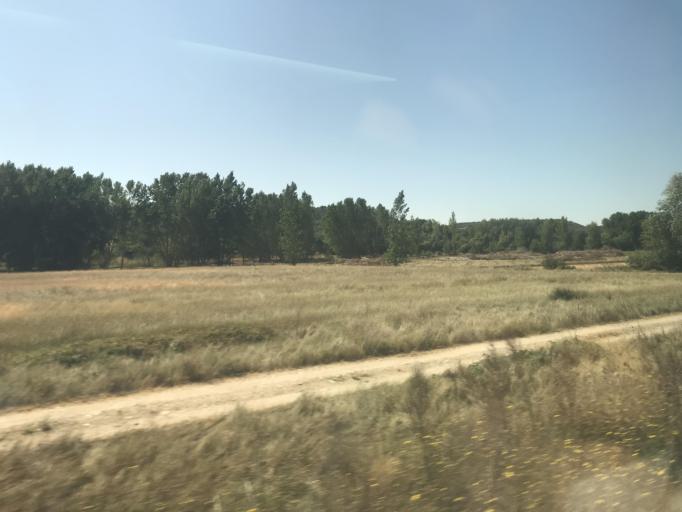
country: ES
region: Castille and Leon
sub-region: Provincia de Burgos
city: Celada del Camino
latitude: 42.2537
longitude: -3.9419
